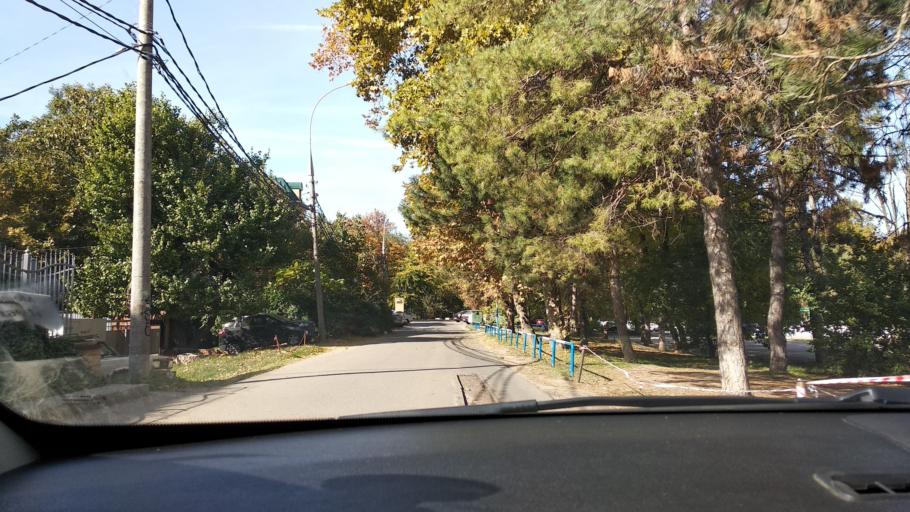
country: RU
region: Adygeya
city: Yablonovskiy
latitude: 45.0165
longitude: 38.9547
